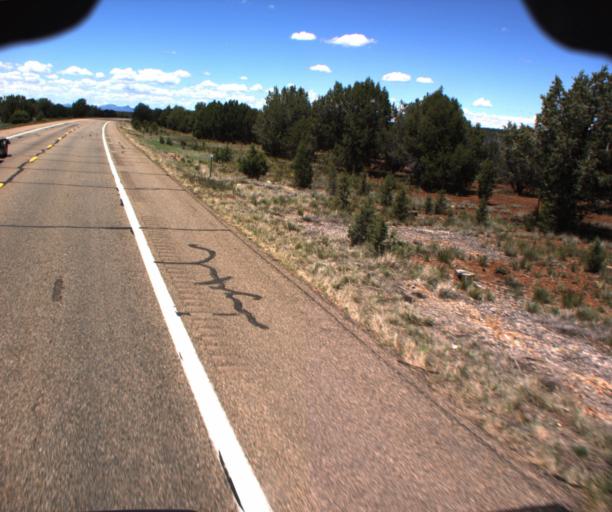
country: US
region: Arizona
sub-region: Yavapai County
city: Paulden
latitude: 35.0938
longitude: -112.4184
